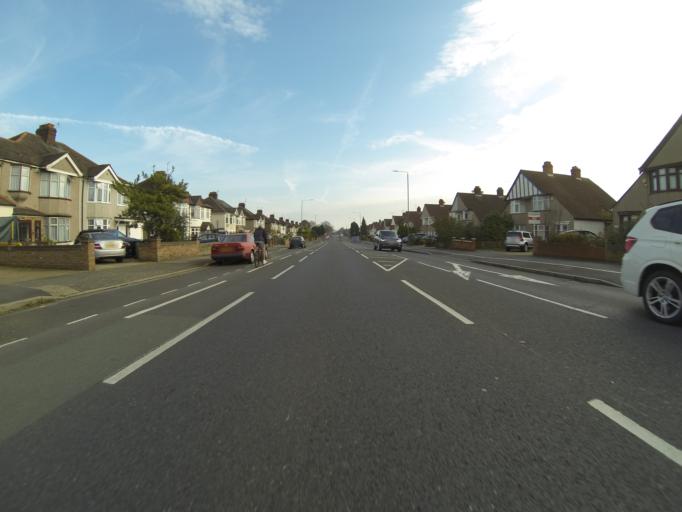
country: GB
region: England
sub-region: Greater London
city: Welling
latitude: 51.4659
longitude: 0.0867
